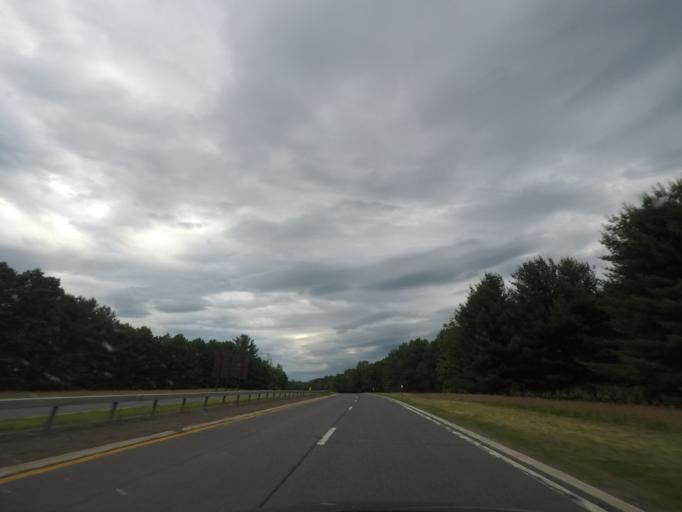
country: US
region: New York
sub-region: Dutchess County
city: Pine Plains
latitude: 42.0302
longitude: -73.7323
